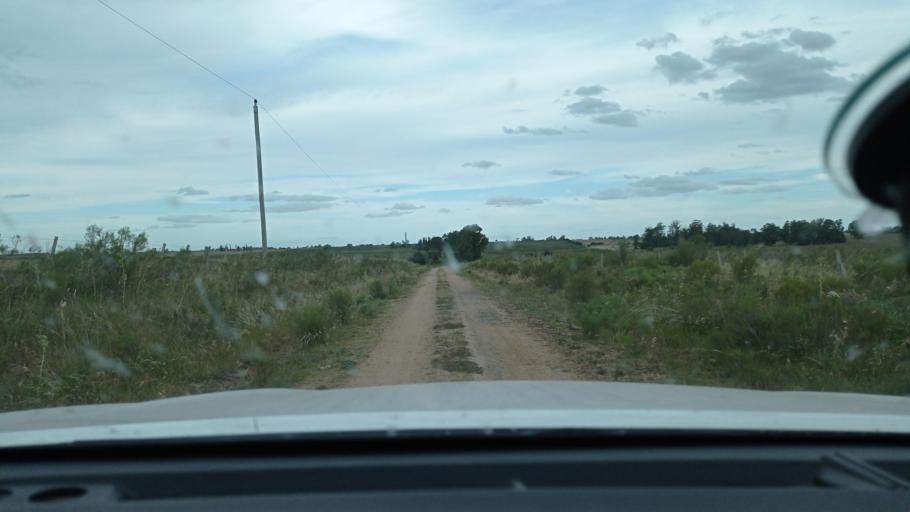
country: UY
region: Florida
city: Casupa
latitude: -34.1403
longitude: -55.8022
